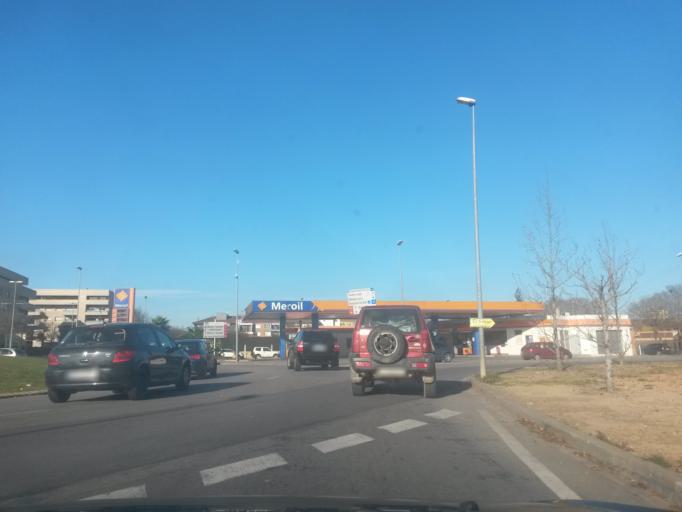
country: ES
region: Catalonia
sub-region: Provincia de Girona
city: Salt
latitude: 41.9668
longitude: 2.7879
